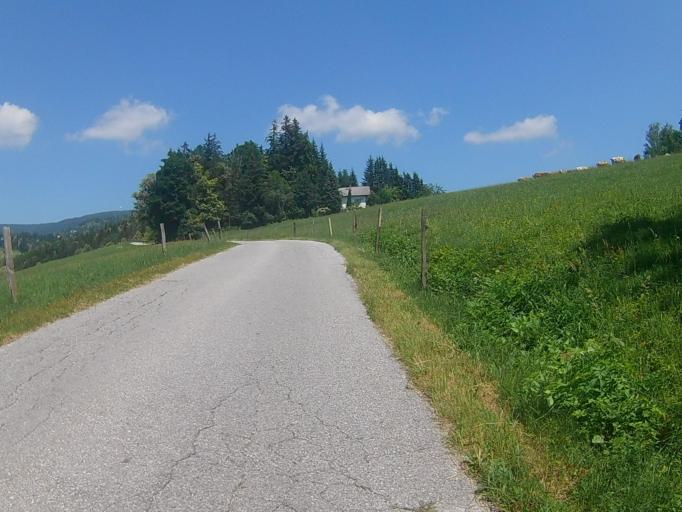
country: SI
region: Race-Fram
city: Morje
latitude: 46.4770
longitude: 15.5880
